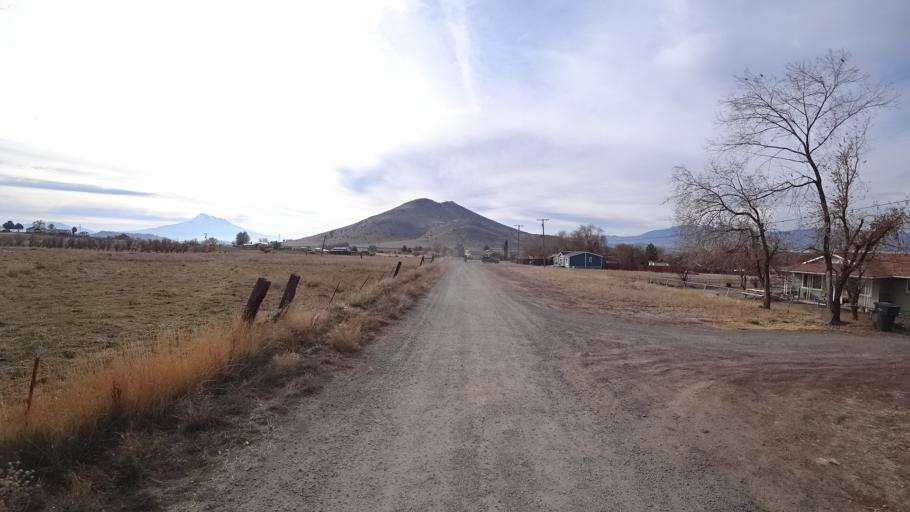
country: US
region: California
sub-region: Siskiyou County
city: Montague
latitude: 41.7285
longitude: -122.5154
